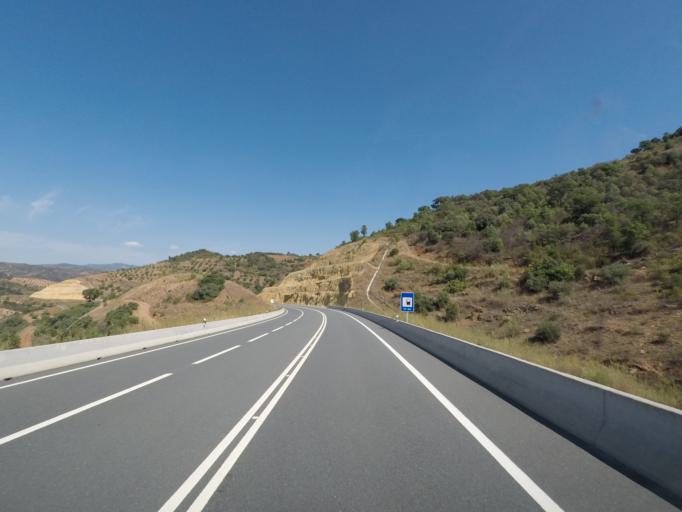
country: PT
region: Braganca
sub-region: Alfandega da Fe
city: Alfandega da Fe
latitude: 41.3005
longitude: -6.8998
